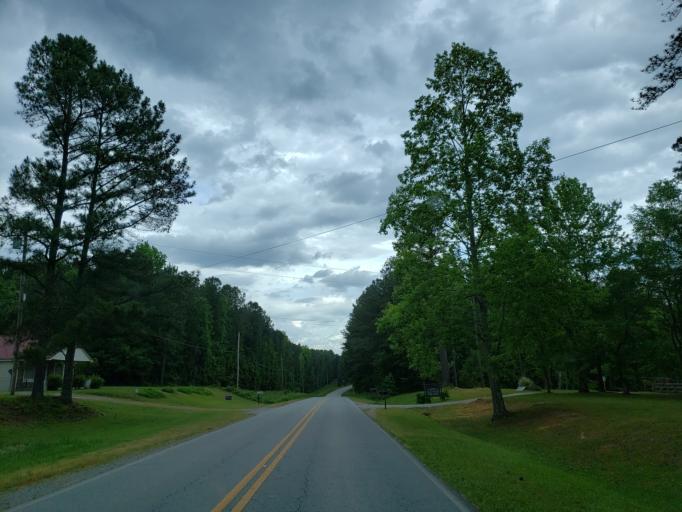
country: US
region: Georgia
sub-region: Polk County
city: Rockmart
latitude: 33.9297
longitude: -85.0553
